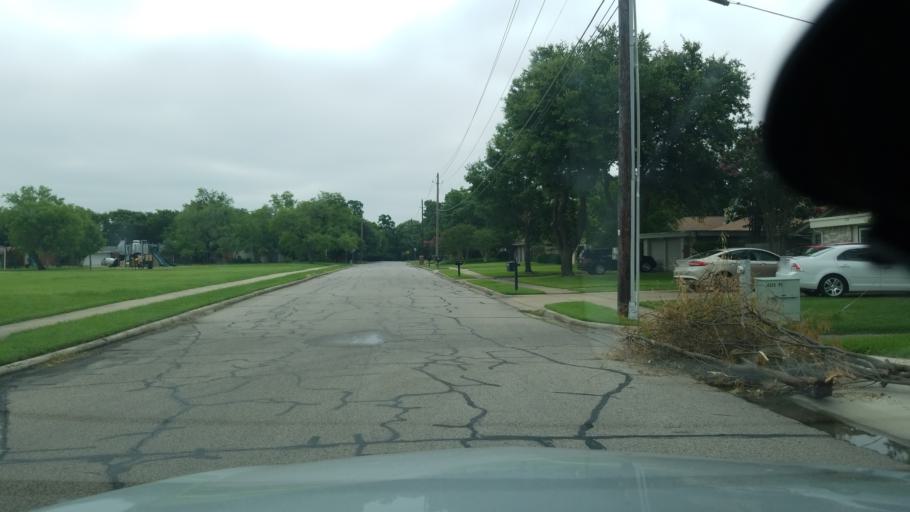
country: US
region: Texas
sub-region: Dallas County
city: Irving
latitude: 32.8520
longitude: -96.9488
